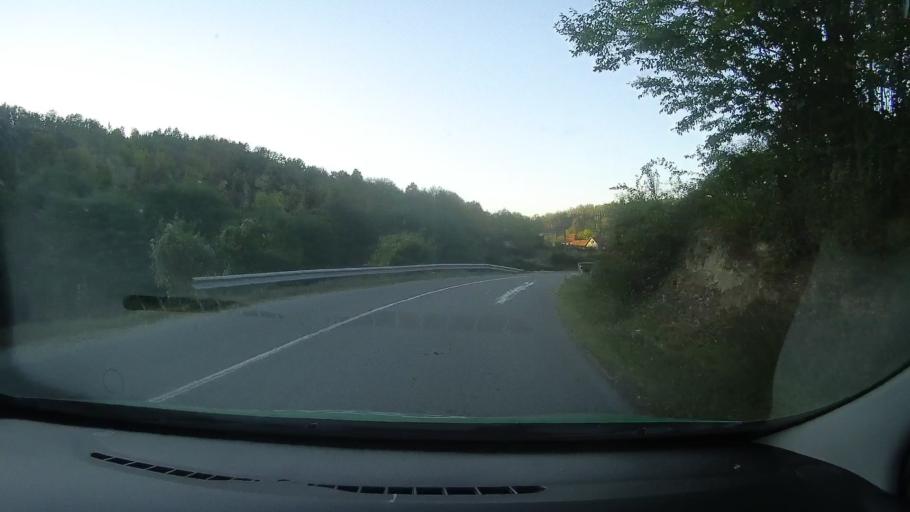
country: RO
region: Timis
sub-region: Comuna Traian Vuia
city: Traian Vuia
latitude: 45.7580
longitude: 22.1041
